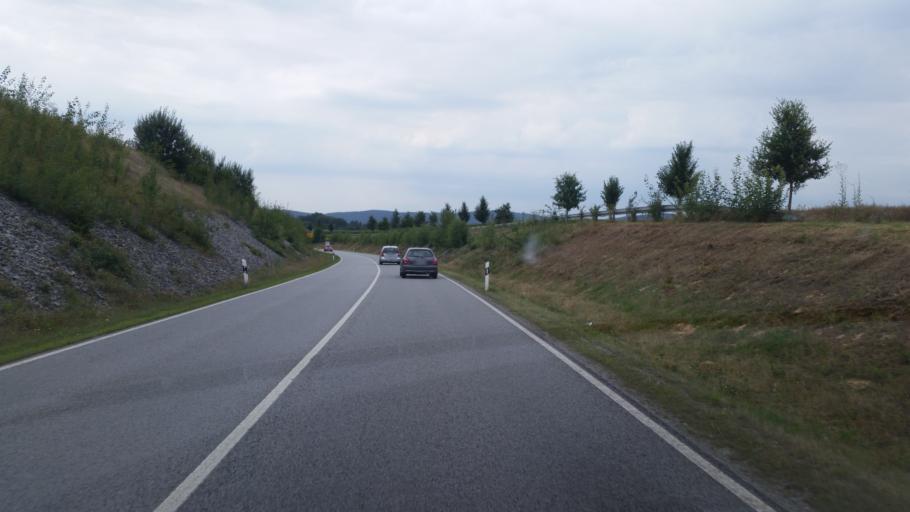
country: DE
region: Saxony
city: Elstra
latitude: 51.2293
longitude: 14.1479
